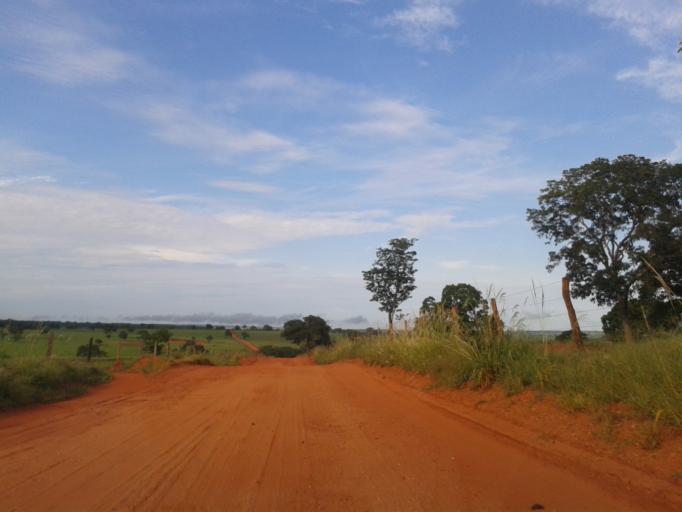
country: BR
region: Minas Gerais
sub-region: Santa Vitoria
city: Santa Vitoria
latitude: -19.0988
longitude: -50.5007
